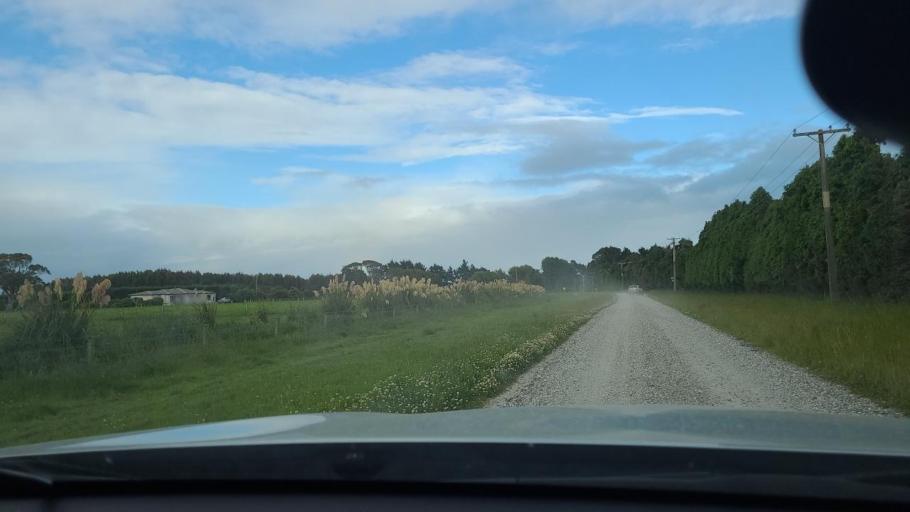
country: NZ
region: Southland
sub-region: Invercargill City
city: Invercargill
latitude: -46.4398
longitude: 168.5966
